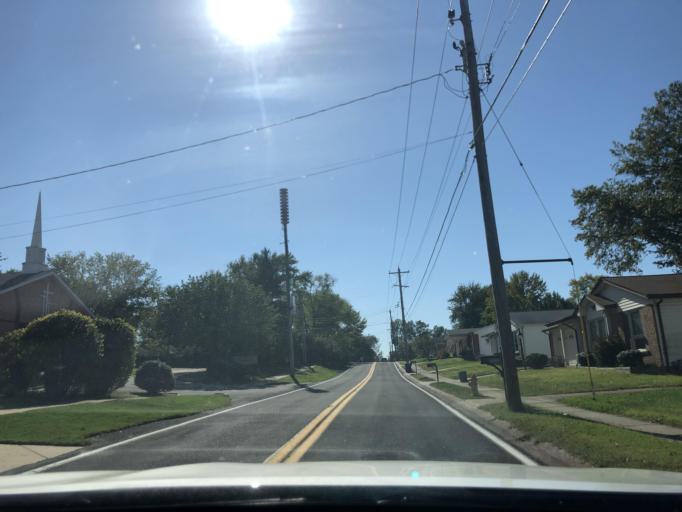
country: US
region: Missouri
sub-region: Saint Louis County
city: Concord
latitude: 38.4914
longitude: -90.3591
